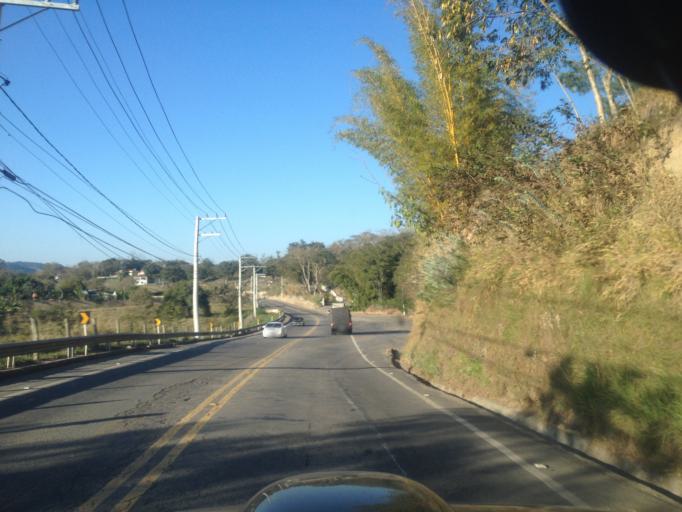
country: BR
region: Rio de Janeiro
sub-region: Porto Real
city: Porto Real
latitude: -22.4227
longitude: -44.2792
